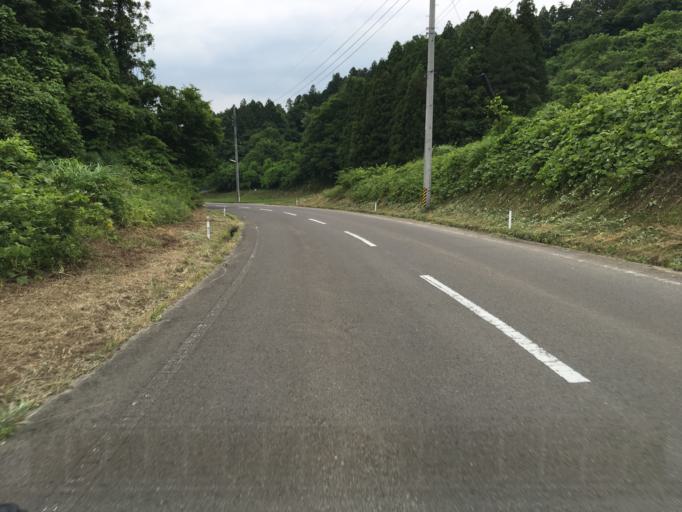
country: JP
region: Fukushima
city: Nihommatsu
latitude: 37.6227
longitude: 140.5244
